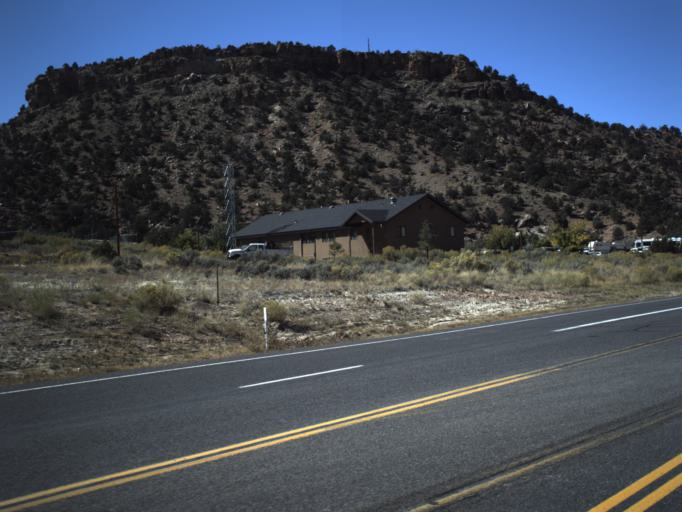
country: US
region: Utah
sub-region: Wayne County
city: Loa
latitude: 37.7728
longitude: -111.6137
